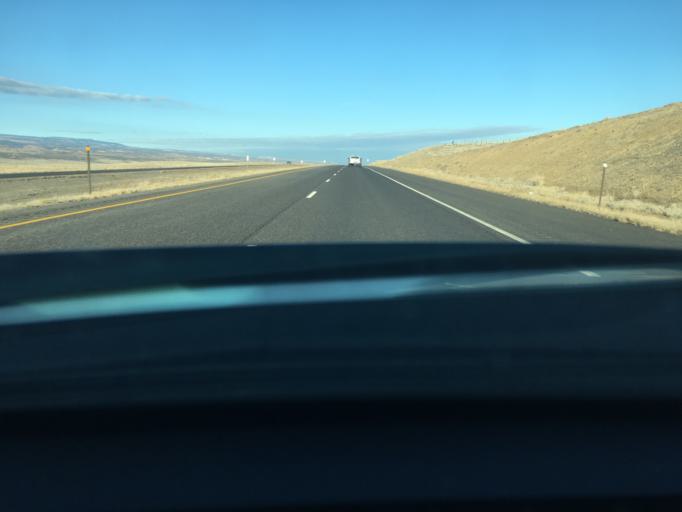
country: US
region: Colorado
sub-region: Mesa County
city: Palisade
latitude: 38.8598
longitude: -108.3183
